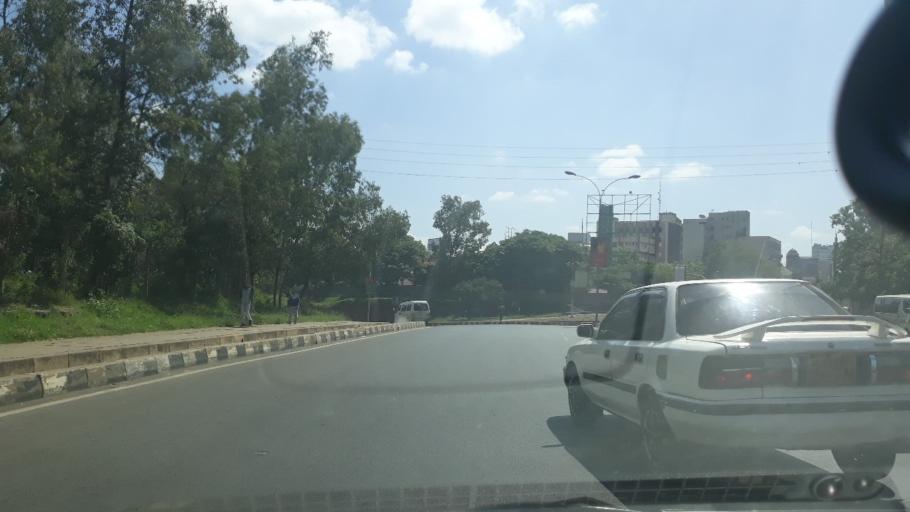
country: KE
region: Nairobi Area
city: Nairobi
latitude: -1.2798
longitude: 36.8188
